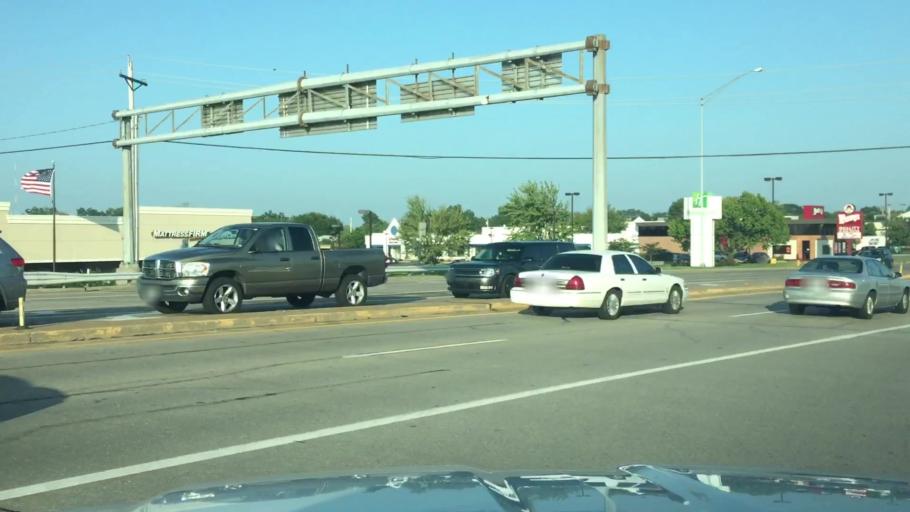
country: US
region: Missouri
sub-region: Saint Louis County
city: Mehlville
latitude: 38.5110
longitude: -90.3354
